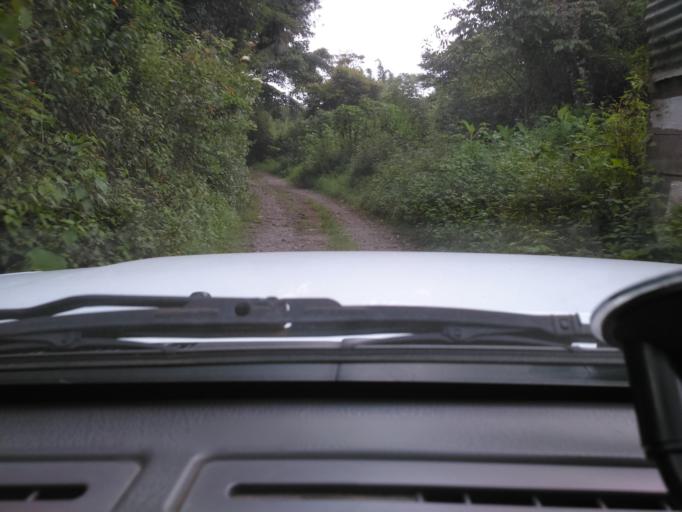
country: MX
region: Veracruz
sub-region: Mariano Escobedo
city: Chicola
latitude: 18.8960
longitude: -97.1098
